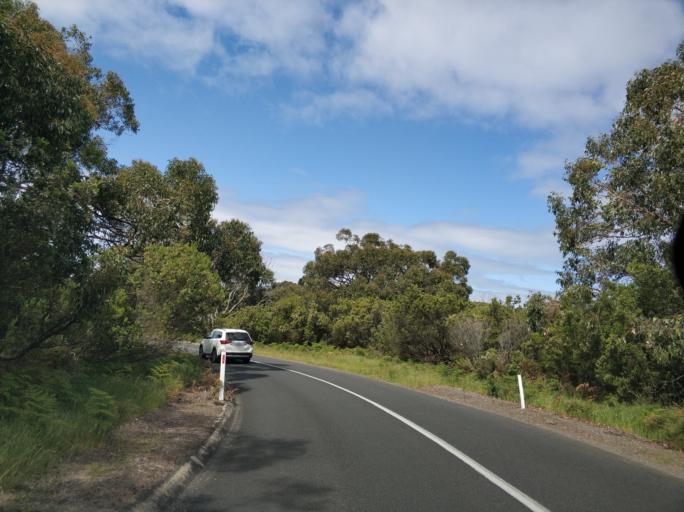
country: AU
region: Victoria
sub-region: Colac-Otway
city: Apollo Bay
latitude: -38.8455
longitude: 143.5328
